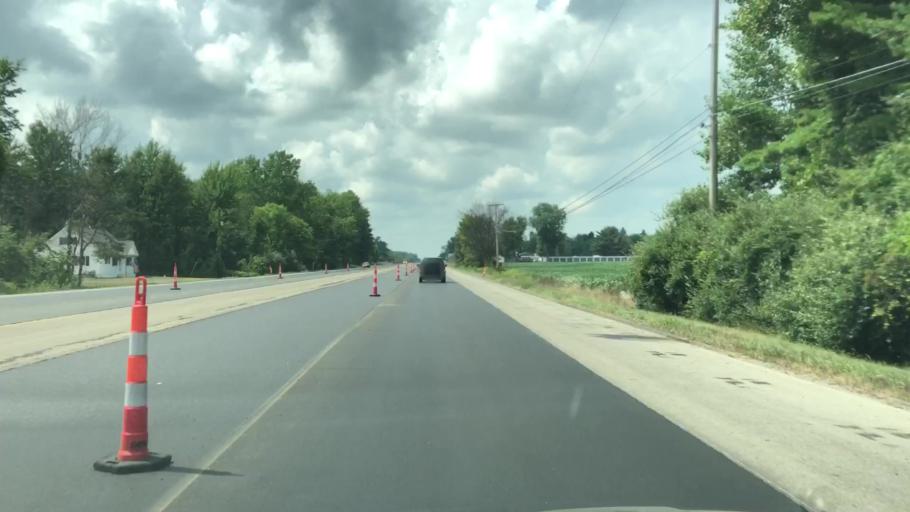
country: US
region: Michigan
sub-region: Isabella County
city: Mount Pleasant
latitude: 43.6117
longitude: -84.6934
